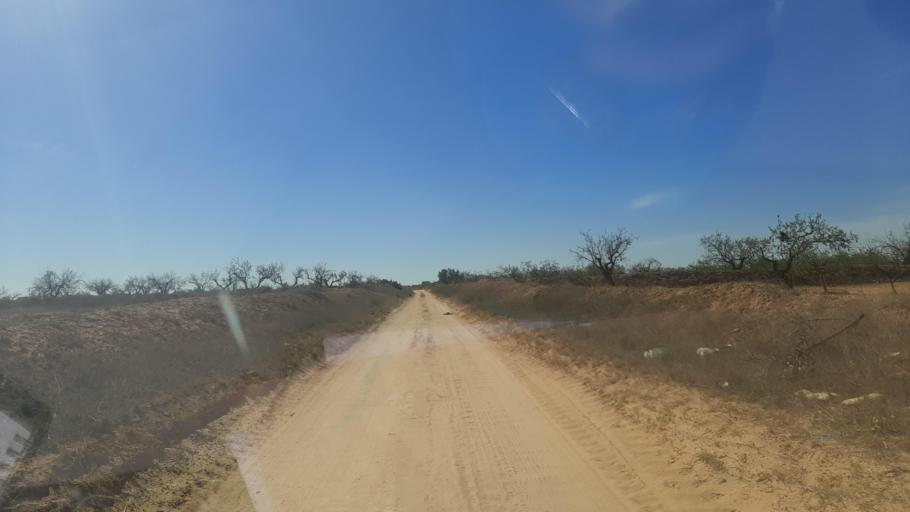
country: TN
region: Safaqis
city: Sfax
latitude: 34.8280
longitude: 10.5553
